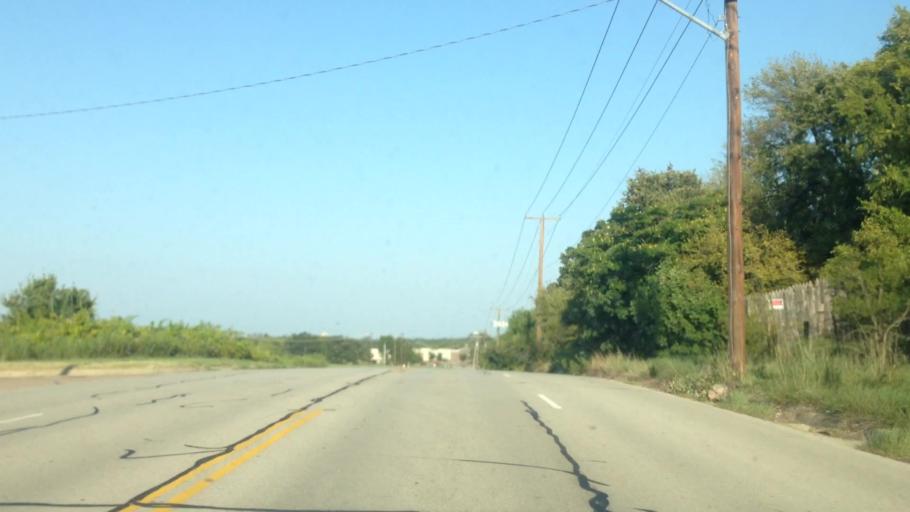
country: US
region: Texas
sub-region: Tarrant County
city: Pantego
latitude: 32.7535
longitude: -97.1785
